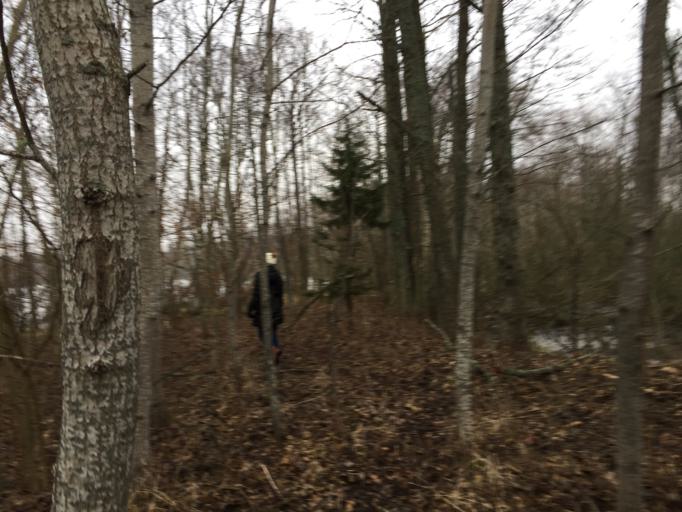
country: EE
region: Saare
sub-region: Kuressaare linn
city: Kuressaare
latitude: 58.1412
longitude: 22.2306
